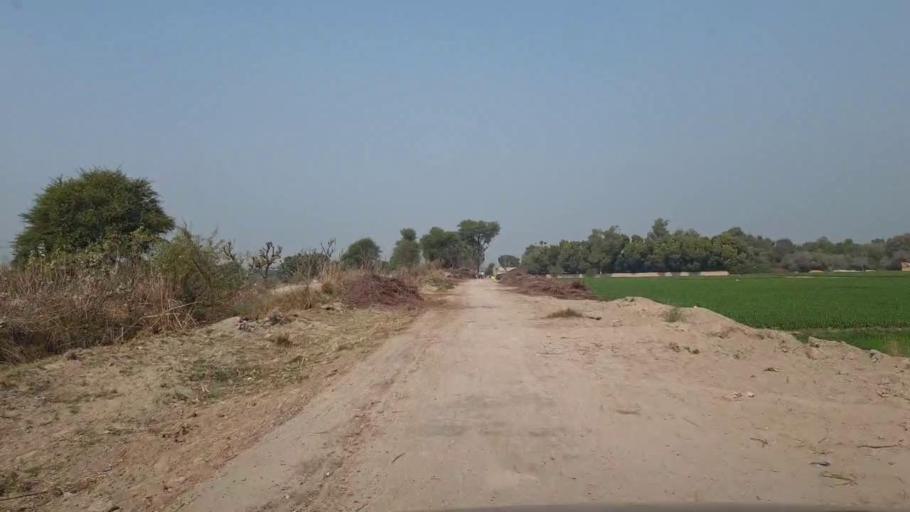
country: PK
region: Sindh
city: Hala
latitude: 25.8415
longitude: 68.4286
